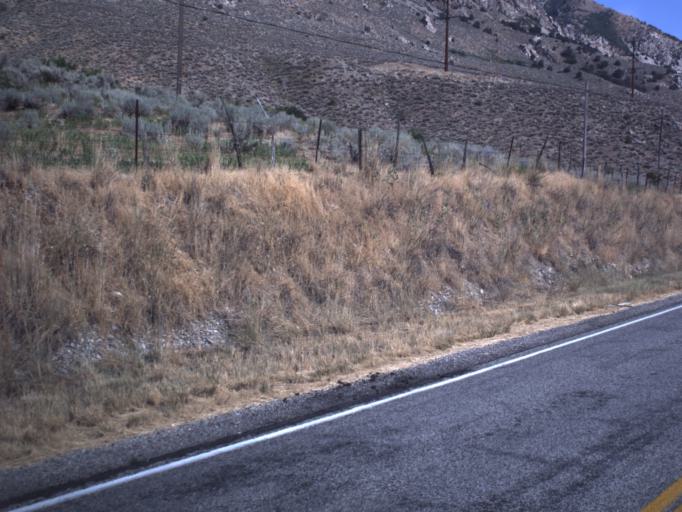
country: US
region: Utah
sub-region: Box Elder County
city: Brigham City
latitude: 41.5586
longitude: -112.0222
